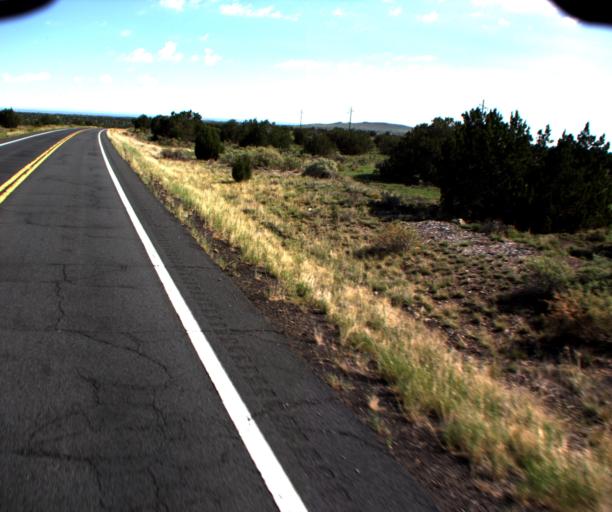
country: US
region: Arizona
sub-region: Coconino County
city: Williams
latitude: 35.5056
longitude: -112.1736
